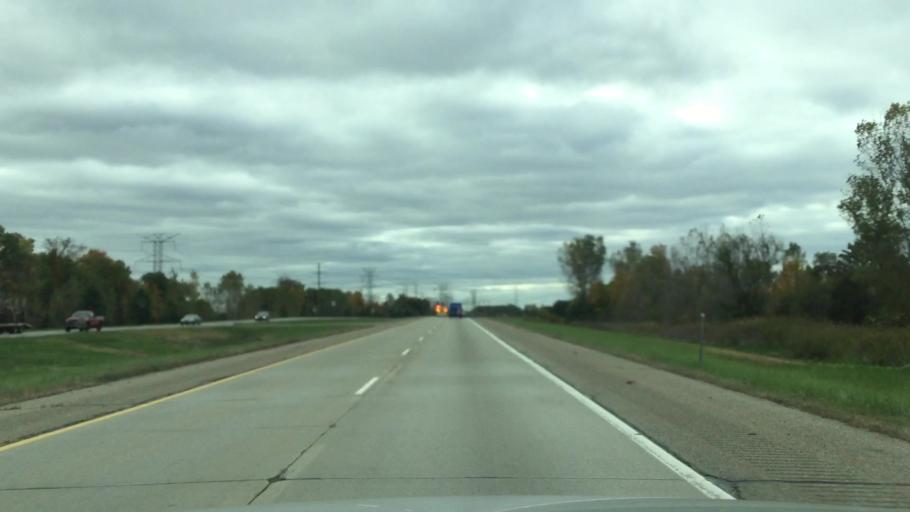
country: US
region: Michigan
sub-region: Macomb County
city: Romeo
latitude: 42.7671
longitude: -83.0093
